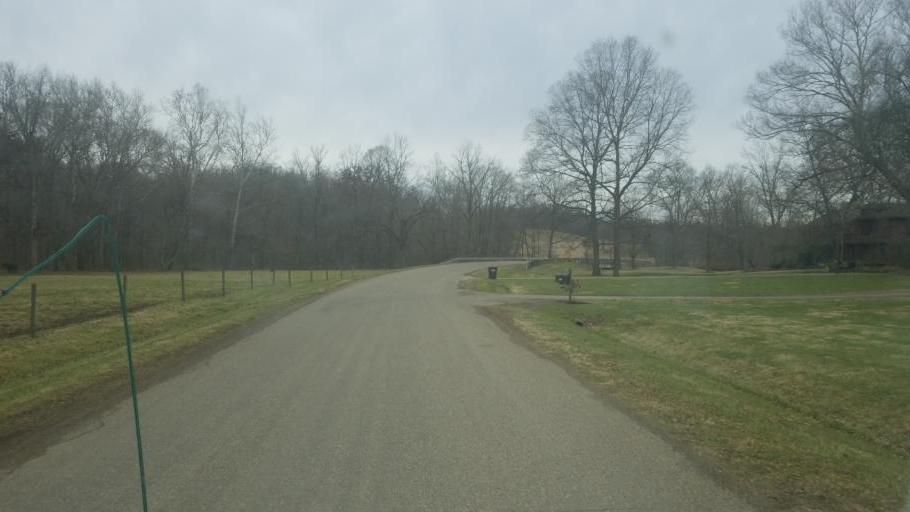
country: US
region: Ohio
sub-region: Richland County
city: Lincoln Heights
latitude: 40.6973
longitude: -82.3894
